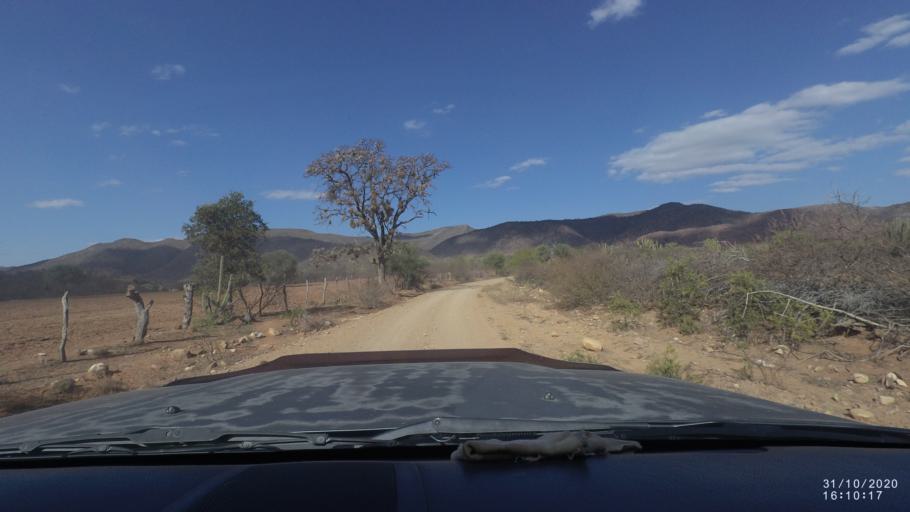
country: BO
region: Chuquisaca
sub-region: Provincia Zudanez
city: Mojocoya
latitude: -18.3832
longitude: -64.6312
